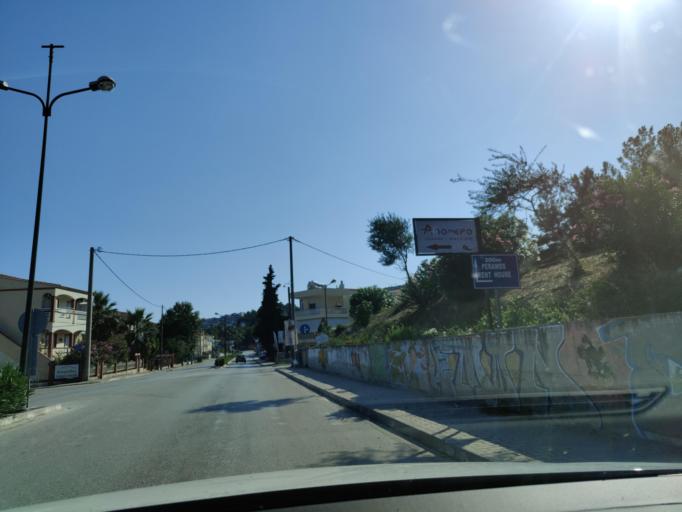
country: GR
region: East Macedonia and Thrace
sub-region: Nomos Kavalas
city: Nea Peramos
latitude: 40.8483
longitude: 24.3091
